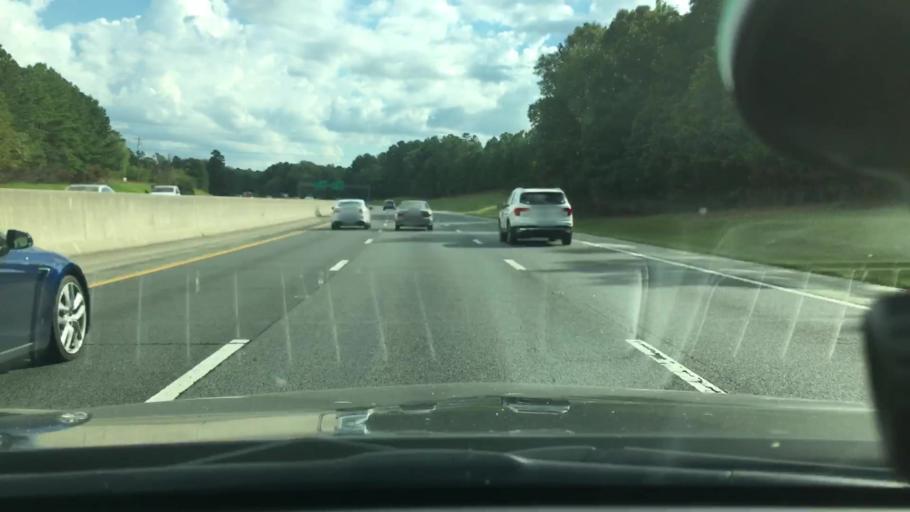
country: US
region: North Carolina
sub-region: Orange County
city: Chapel Hill
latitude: 35.9194
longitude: -78.9852
